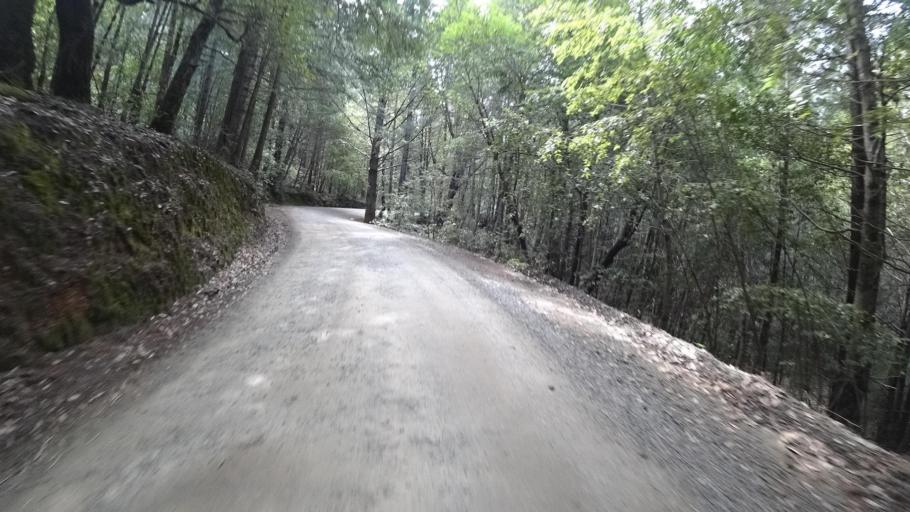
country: US
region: California
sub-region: Humboldt County
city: Redway
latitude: 40.0329
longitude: -123.8367
